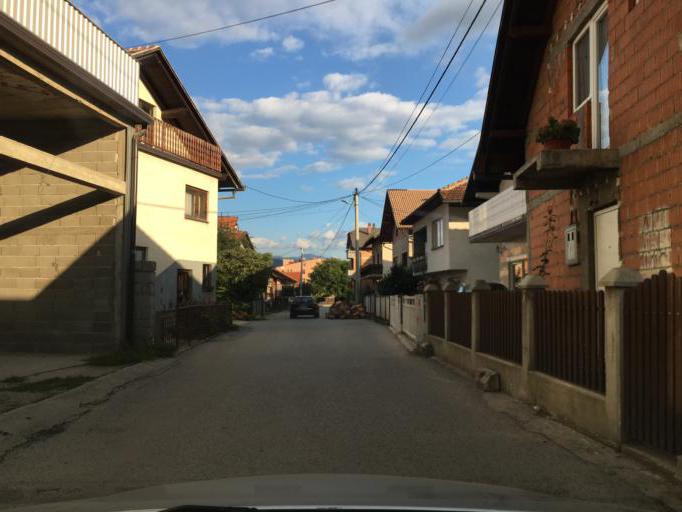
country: BA
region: Federation of Bosnia and Herzegovina
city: Bugojno
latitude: 44.0551
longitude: 17.4518
